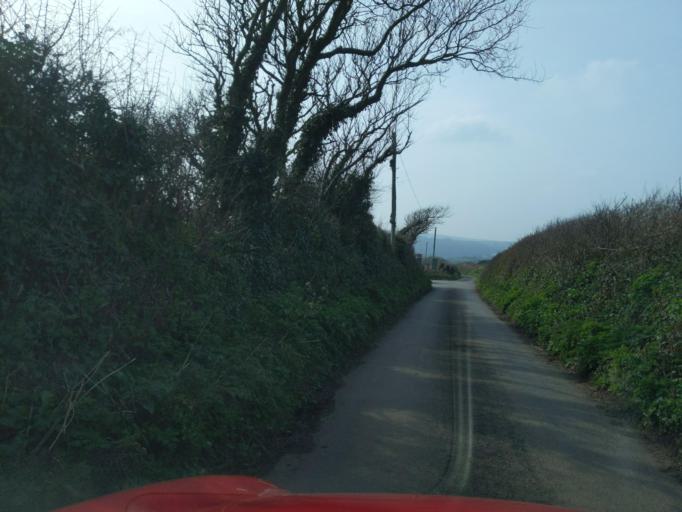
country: GB
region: England
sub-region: Devon
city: Salcombe
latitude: 50.2242
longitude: -3.7486
